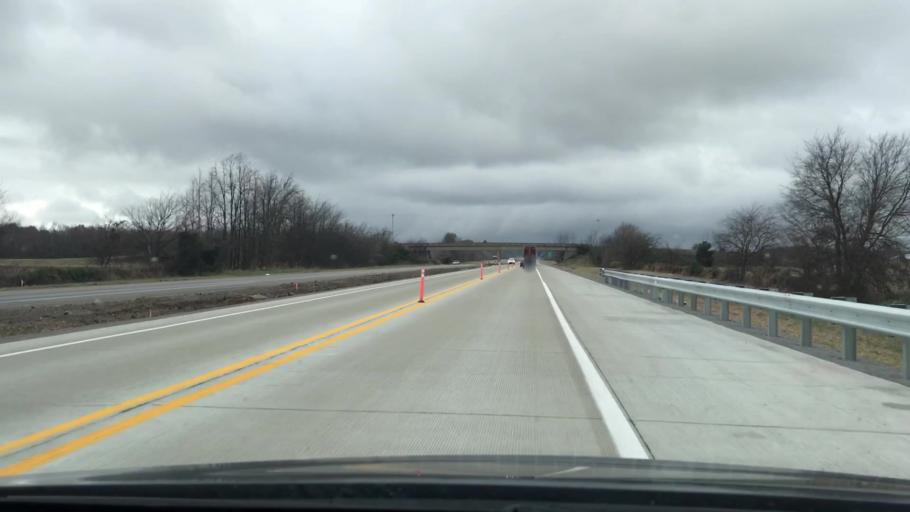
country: US
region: Kentucky
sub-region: Hopkins County
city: Nortonville
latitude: 37.0270
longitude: -87.4592
